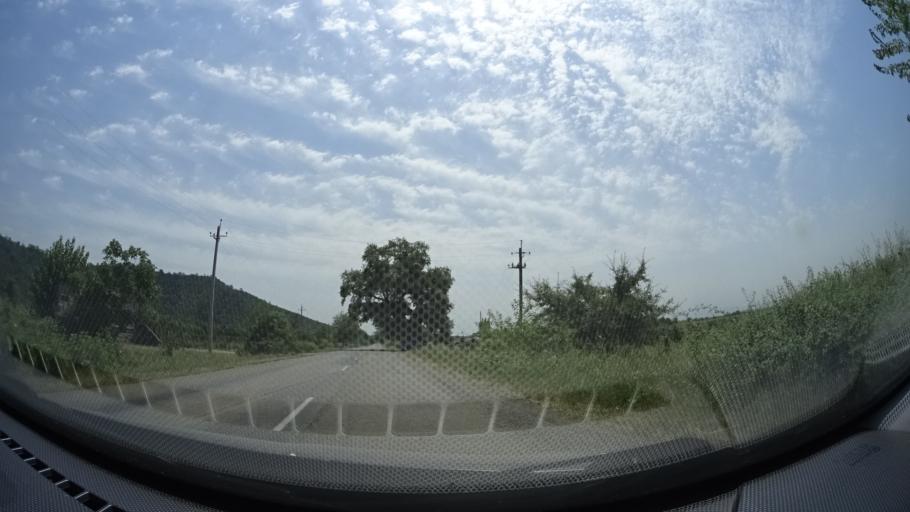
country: GE
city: Bagdadi
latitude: 41.8630
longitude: 46.0192
